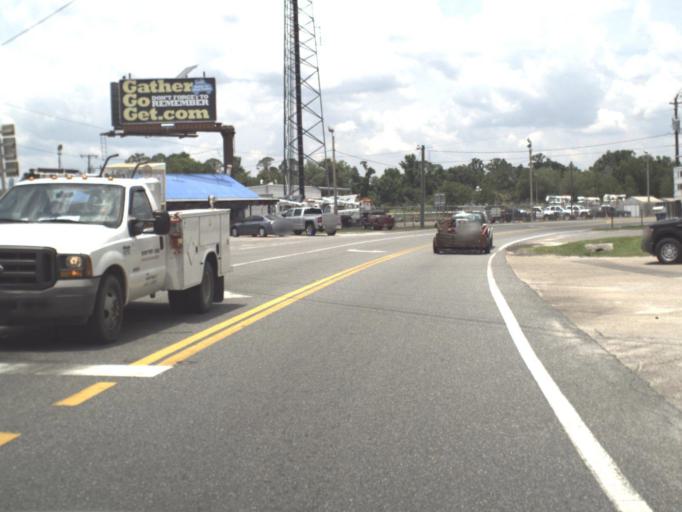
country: US
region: Florida
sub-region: Columbia County
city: Watertown
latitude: 30.1866
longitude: -82.6040
